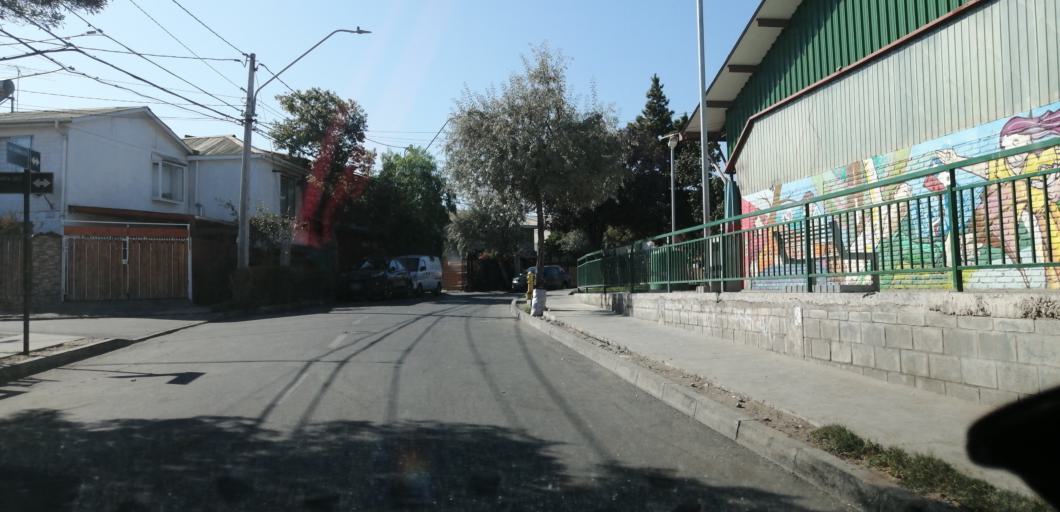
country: CL
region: Santiago Metropolitan
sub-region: Provincia de Santiago
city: Lo Prado
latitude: -33.4453
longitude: -70.7698
